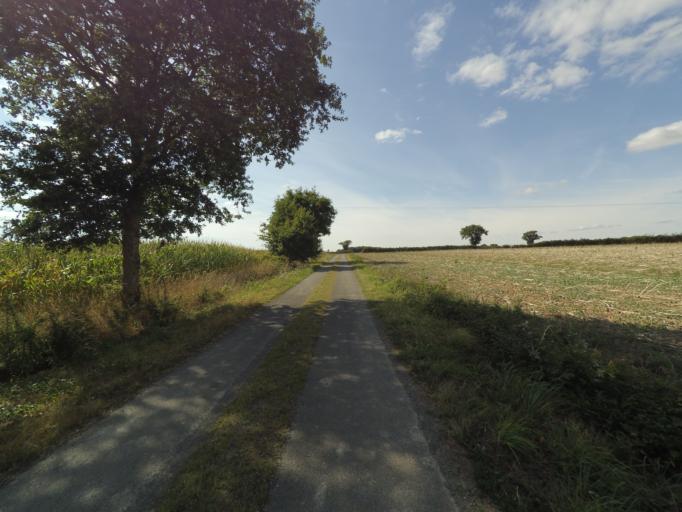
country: FR
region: Pays de la Loire
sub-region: Departement de la Loire-Atlantique
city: Vieillevigne
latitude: 46.9570
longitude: -1.4445
